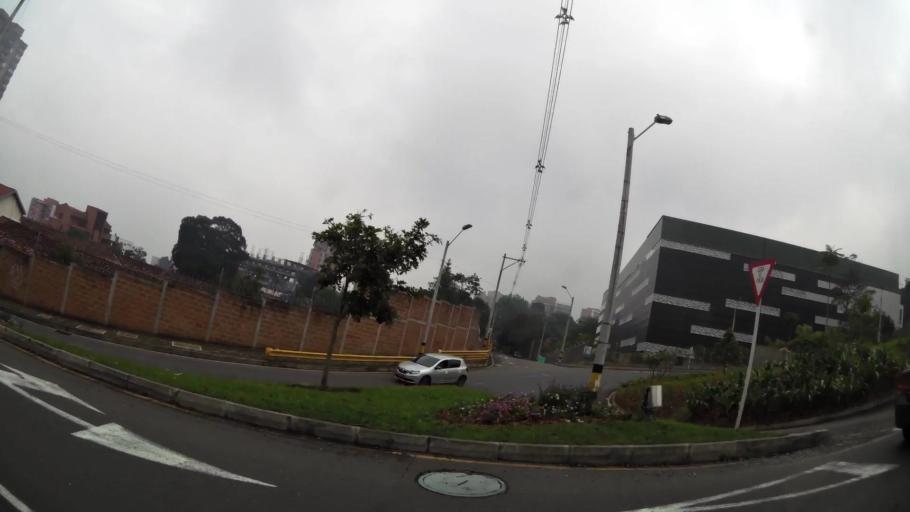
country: CO
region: Antioquia
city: Envigado
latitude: 6.1865
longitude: -75.5608
